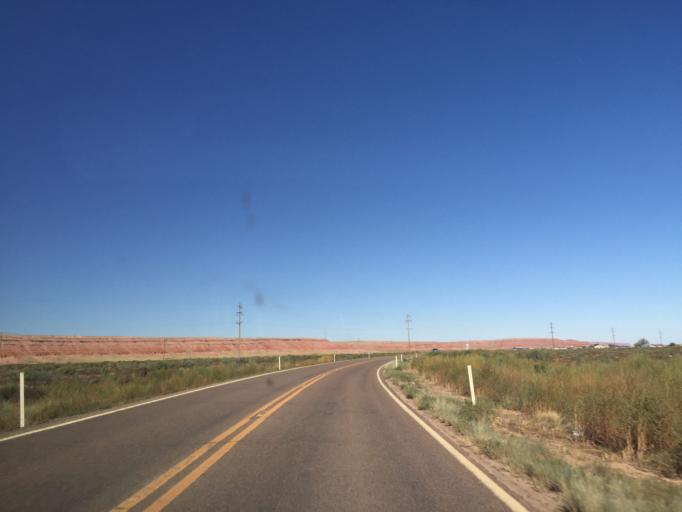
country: US
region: Arizona
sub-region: Apache County
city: Many Farms
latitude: 36.3340
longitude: -109.6239
